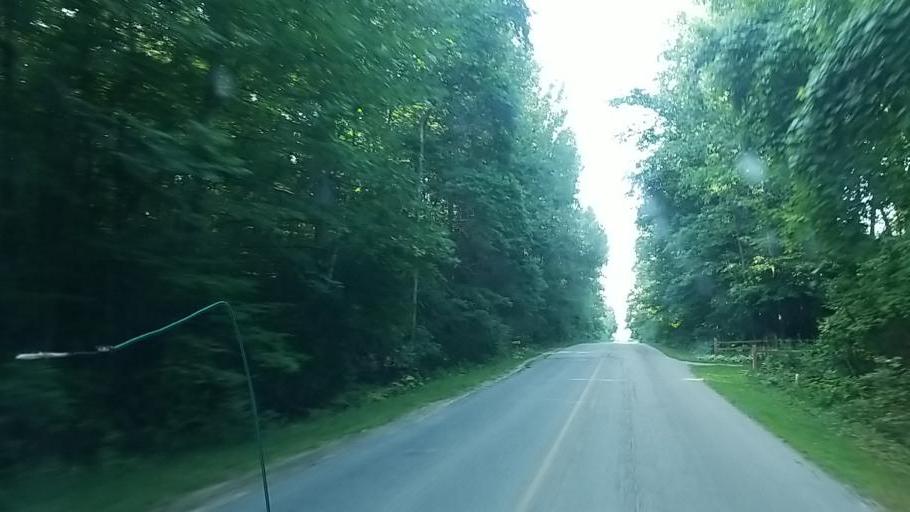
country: US
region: Michigan
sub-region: Newaygo County
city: Newaygo
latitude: 43.3741
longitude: -85.8307
